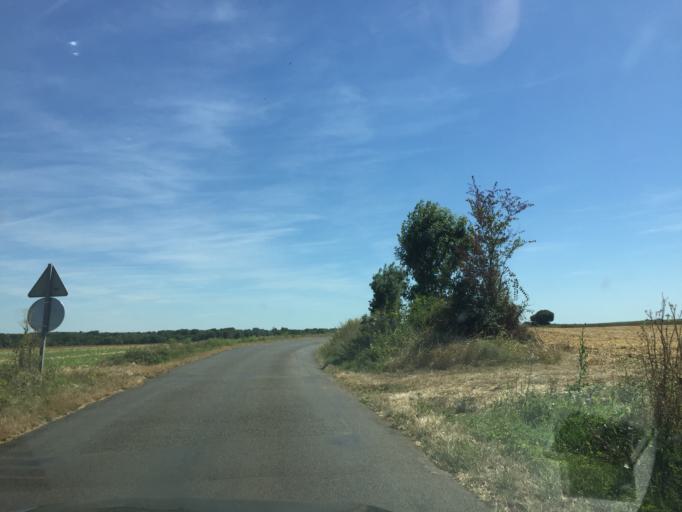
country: FR
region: Poitou-Charentes
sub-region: Departement de la Vienne
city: Vivonne
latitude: 46.4395
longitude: 0.2926
